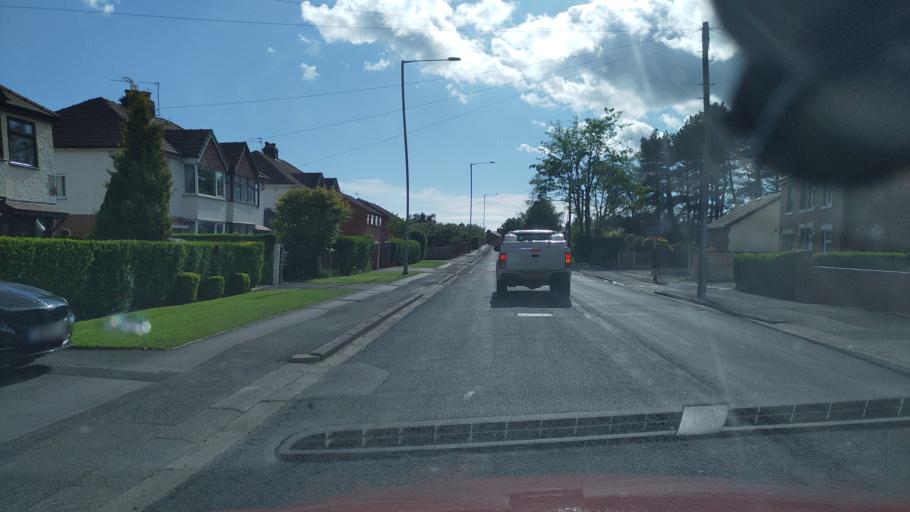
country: GB
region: England
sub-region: Lancashire
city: Leyland
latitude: 53.7279
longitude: -2.6764
